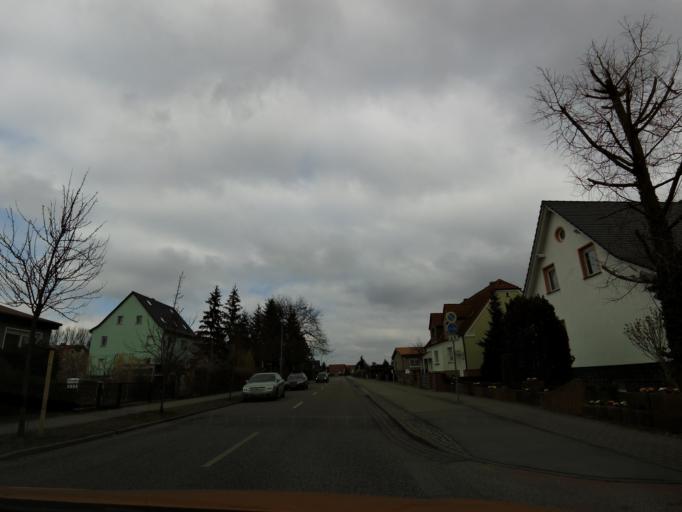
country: DE
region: Brandenburg
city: Rathenow
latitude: 52.6170
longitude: 12.3408
